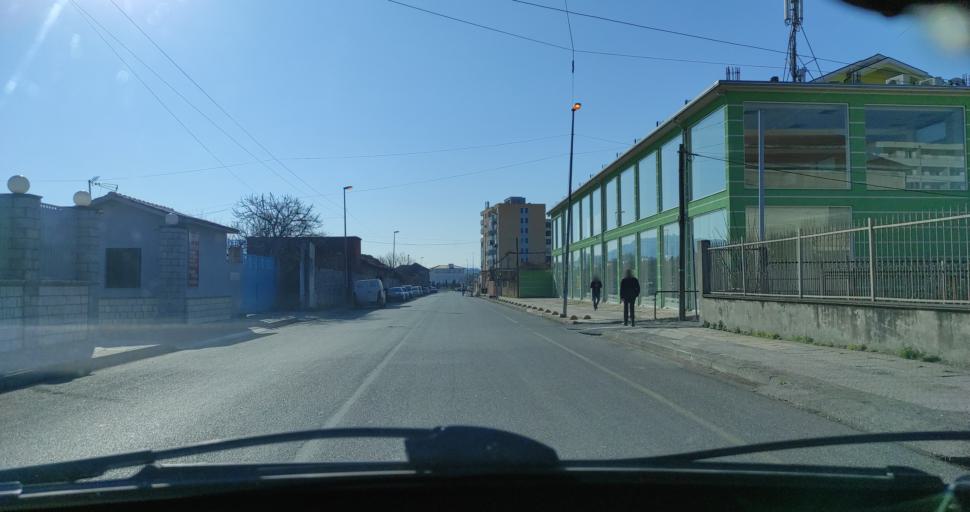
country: AL
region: Shkoder
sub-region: Rrethi i Shkodres
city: Shkoder
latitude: 42.0777
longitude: 19.5230
